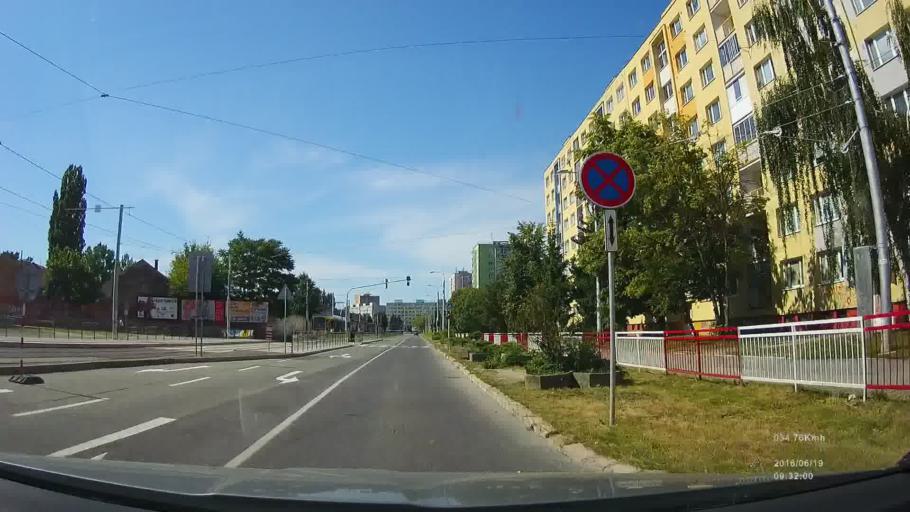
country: SK
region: Kosicky
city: Kosice
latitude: 48.7258
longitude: 21.2497
